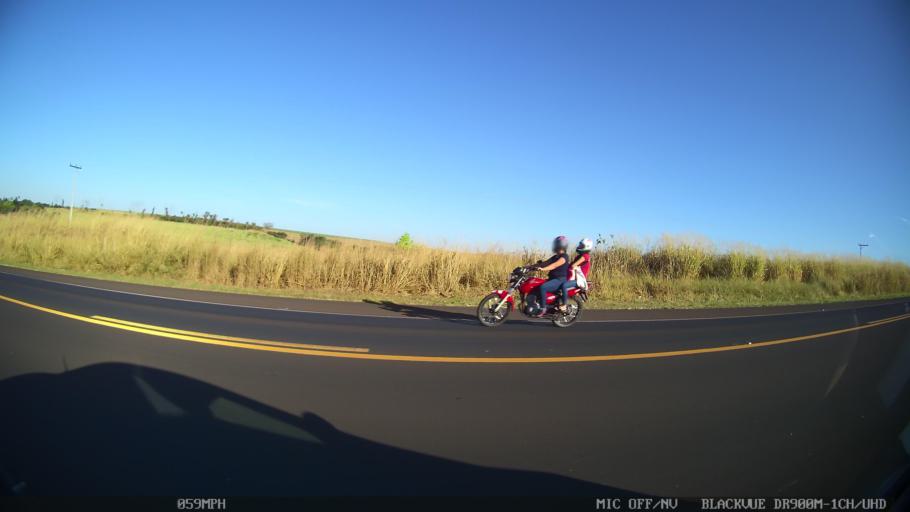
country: BR
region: Sao Paulo
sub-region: Guapiacu
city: Guapiacu
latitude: -20.7465
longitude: -49.1188
